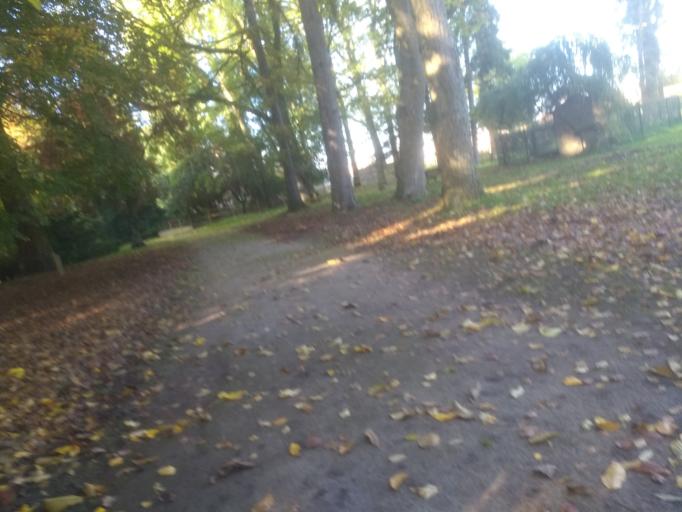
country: FR
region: Nord-Pas-de-Calais
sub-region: Departement du Pas-de-Calais
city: Tilloy-les-Mofflaines
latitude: 50.2753
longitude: 2.8206
